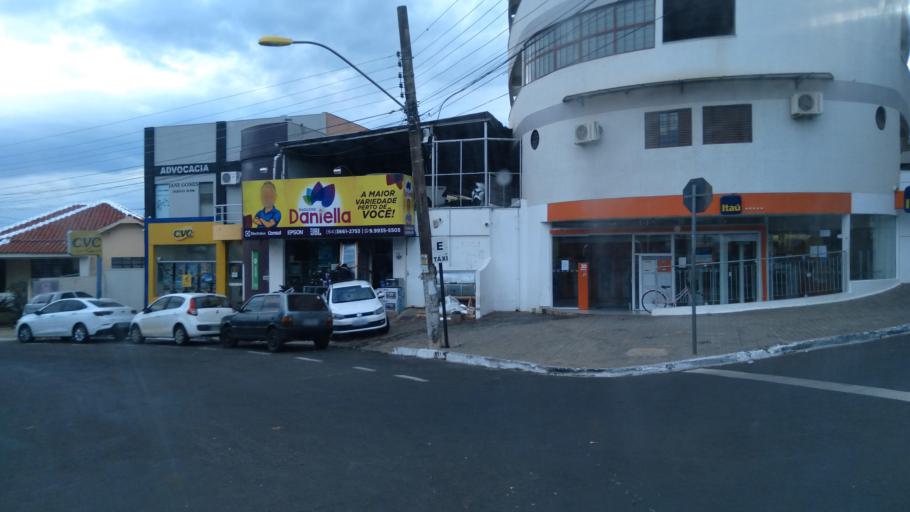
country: BR
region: Goias
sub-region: Mineiros
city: Mineiros
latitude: -17.5688
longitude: -52.5560
